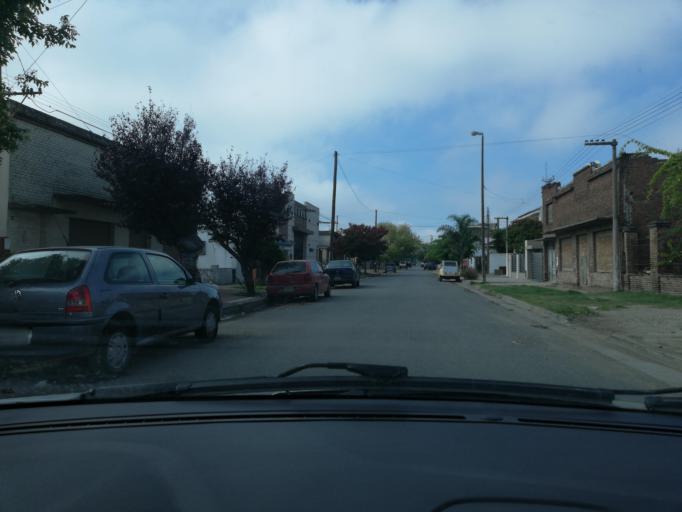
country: AR
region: Buenos Aires
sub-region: Partido de Balcarce
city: Balcarce
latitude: -37.8397
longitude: -58.2601
